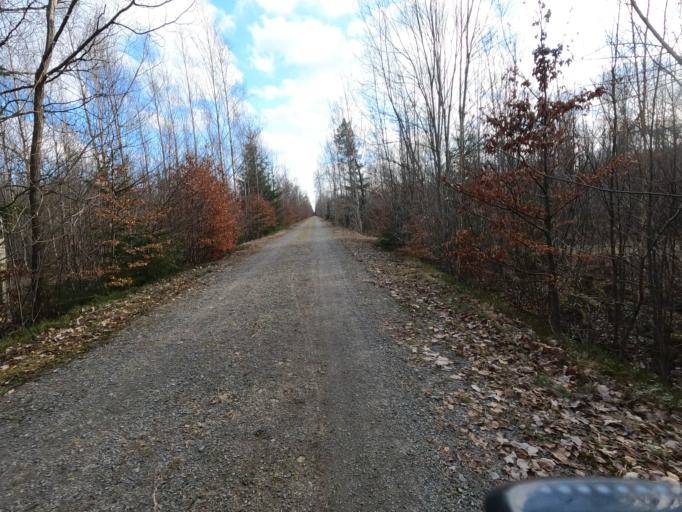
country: SE
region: Kronoberg
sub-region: Vaxjo Kommun
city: Gemla
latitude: 56.6576
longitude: 14.6189
